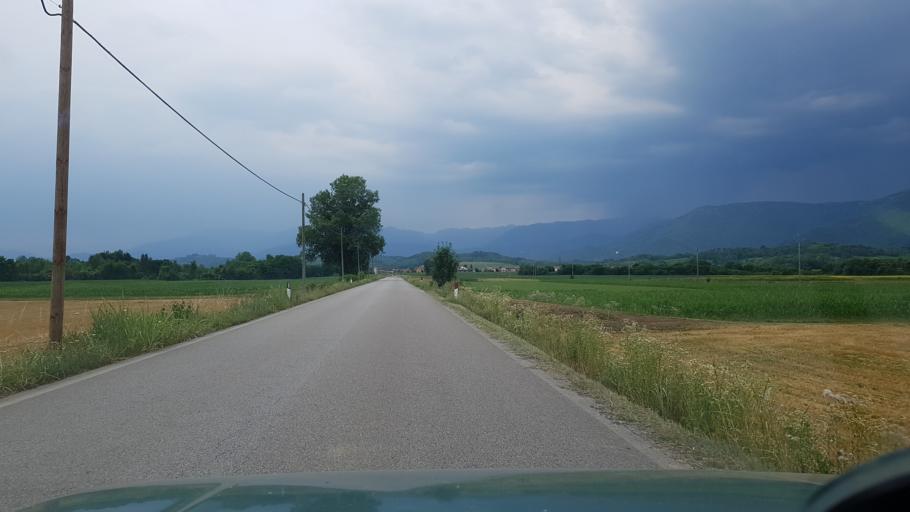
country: IT
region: Friuli Venezia Giulia
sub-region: Provincia di Udine
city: Faedis
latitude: 46.1283
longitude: 13.3217
